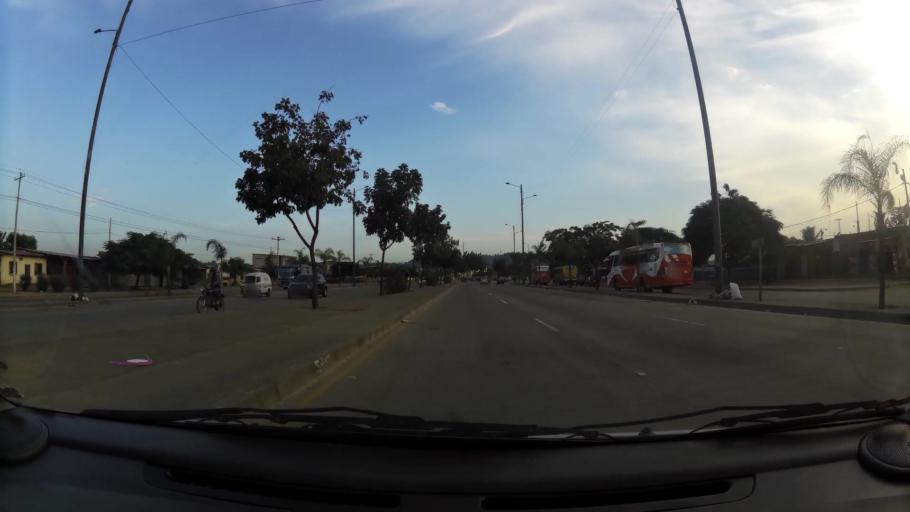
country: EC
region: Guayas
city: Eloy Alfaro
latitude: -2.0871
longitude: -79.8964
